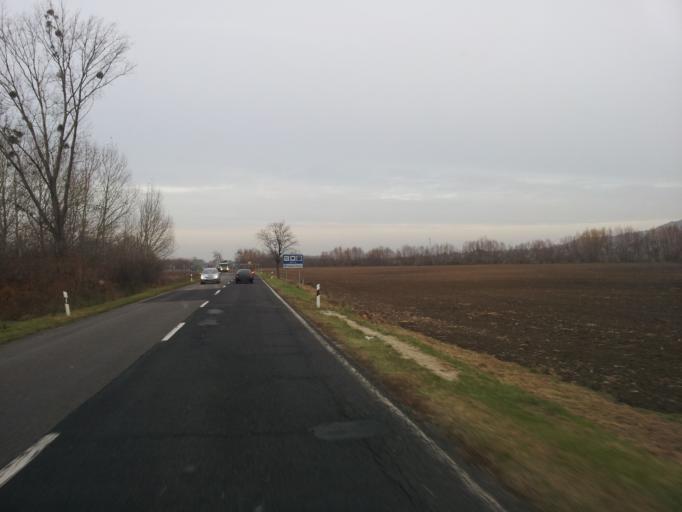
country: HU
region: Veszprem
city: Devecser
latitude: 47.1239
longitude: 17.3794
